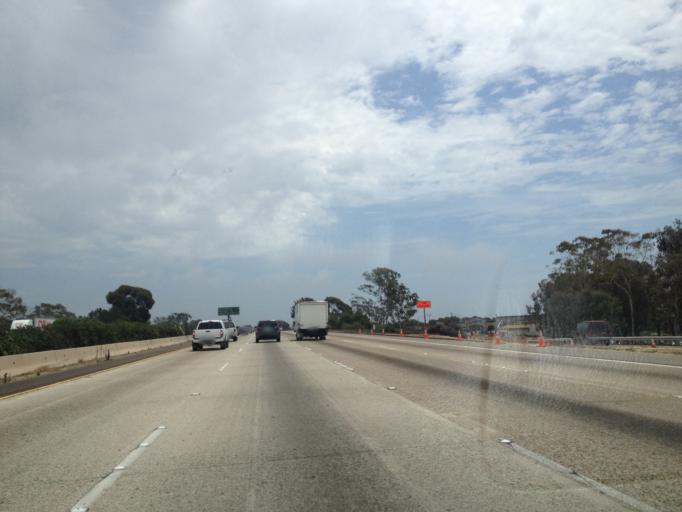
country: US
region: California
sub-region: San Diego County
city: Encinitas
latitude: 33.0383
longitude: -117.2829
